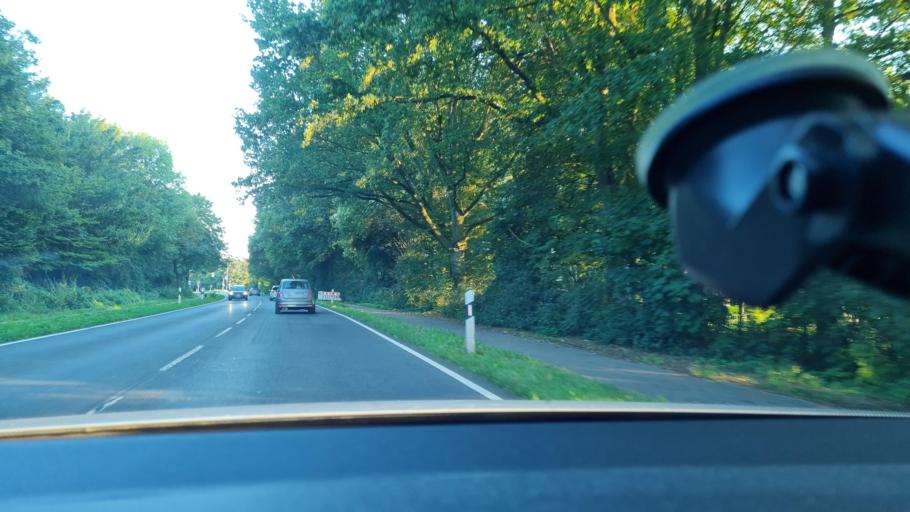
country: DE
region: North Rhine-Westphalia
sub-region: Regierungsbezirk Dusseldorf
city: Dinslaken
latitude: 51.5601
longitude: 6.7700
